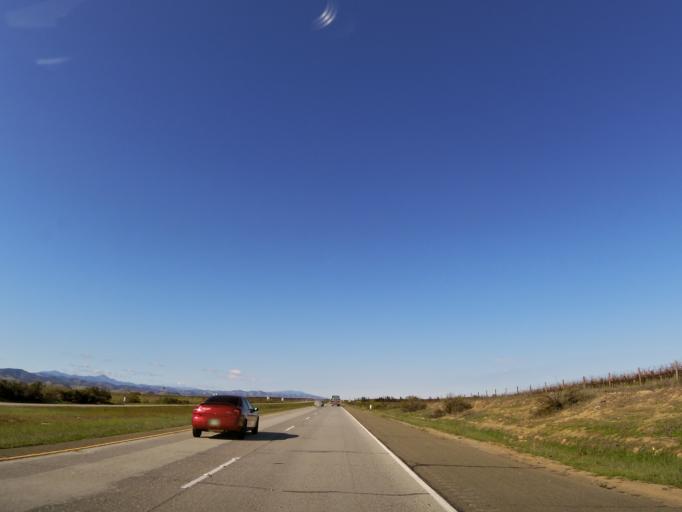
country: US
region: California
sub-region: Monterey County
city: King City
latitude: 36.0551
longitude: -120.9719
